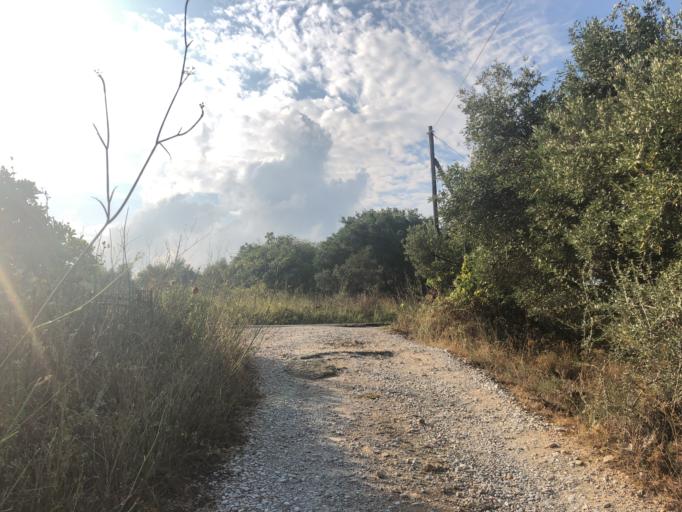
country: GR
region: Crete
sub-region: Nomos Chanias
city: Georgioupolis
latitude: 35.3465
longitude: 24.3072
